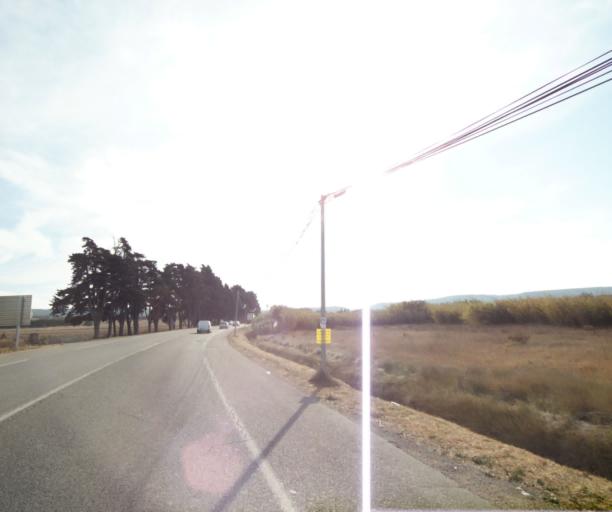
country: FR
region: Provence-Alpes-Cote d'Azur
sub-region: Departement des Bouches-du-Rhone
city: Chateauneuf-les-Martigues
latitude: 43.3926
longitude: 5.1937
